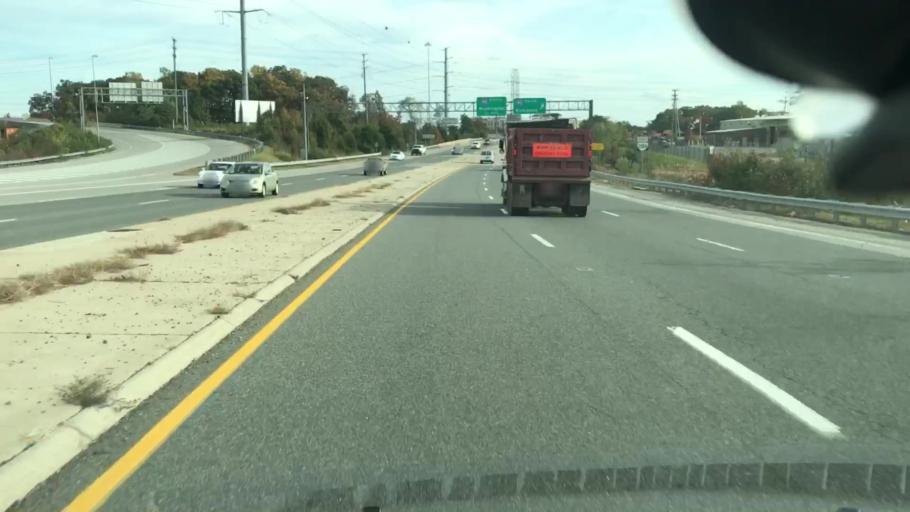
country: US
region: Virginia
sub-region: Fairfax County
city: Newington
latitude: 38.7440
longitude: -77.1926
